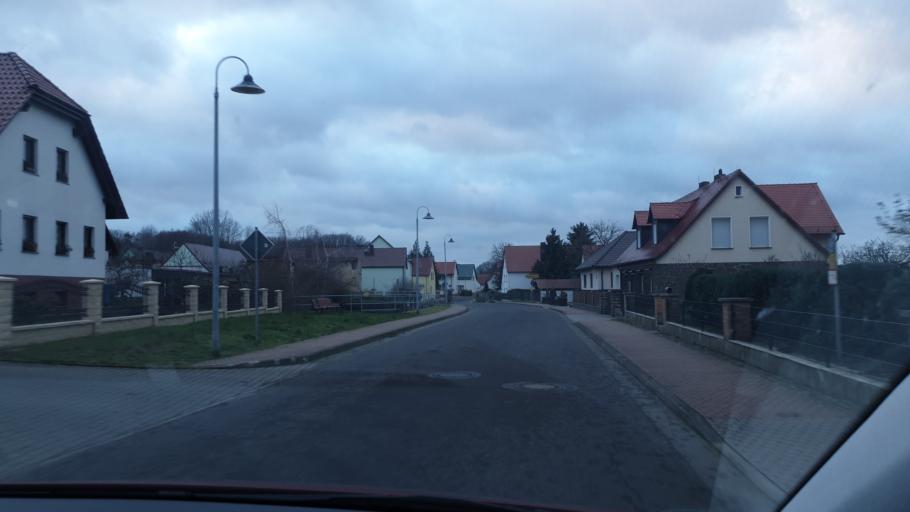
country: DE
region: Saxony
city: Falkenhain
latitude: 51.4524
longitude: 12.8702
